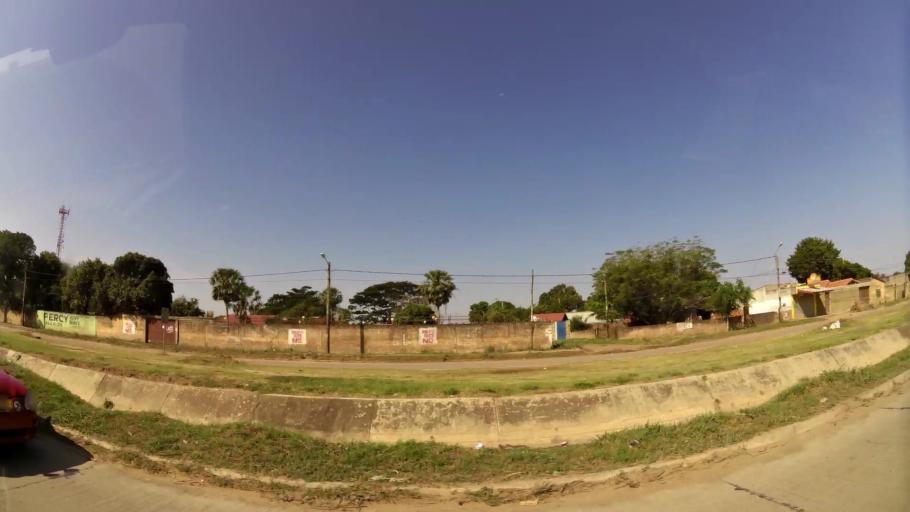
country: BO
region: Santa Cruz
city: Cotoca
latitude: -17.7693
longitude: -63.1076
